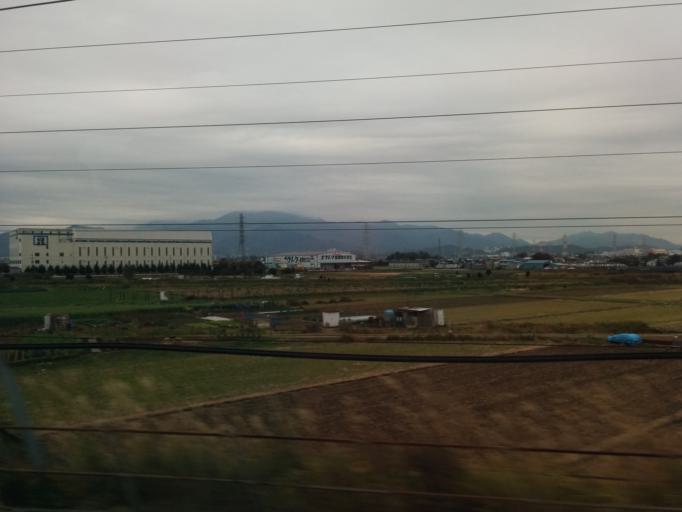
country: JP
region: Kanagawa
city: Isehara
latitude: 35.3815
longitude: 139.3563
